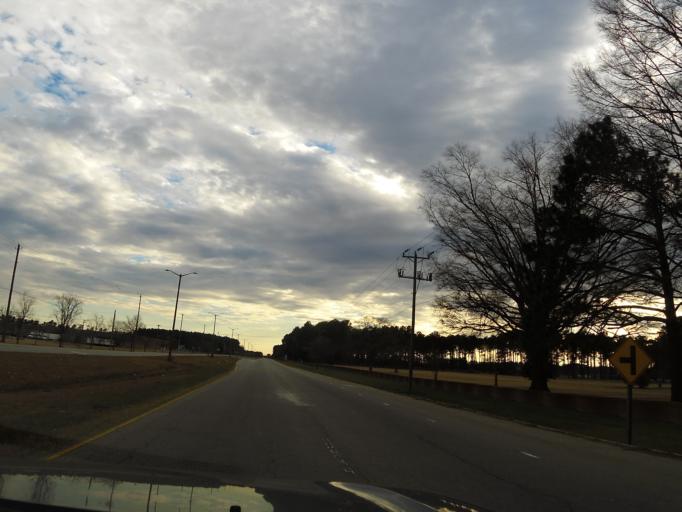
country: US
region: North Carolina
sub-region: Nash County
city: Rocky Mount
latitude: 36.0177
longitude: -77.7707
